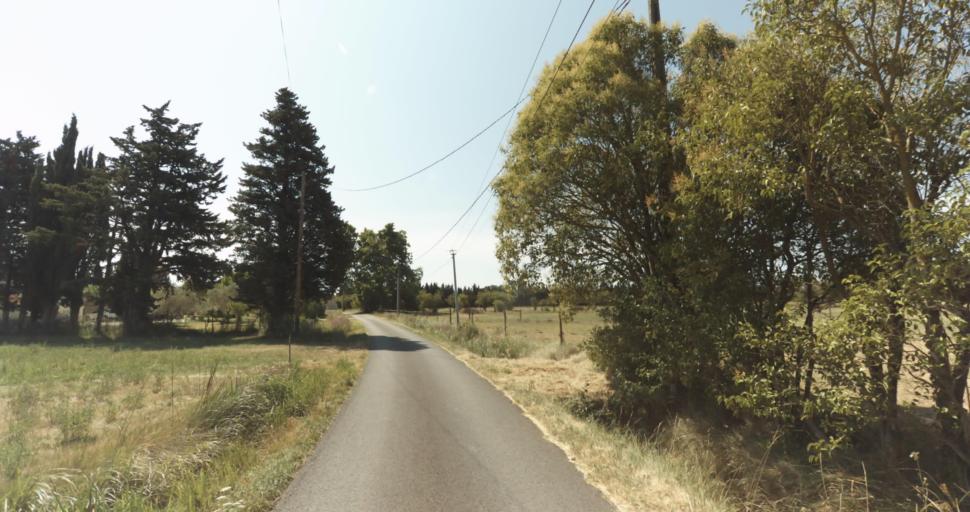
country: FR
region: Provence-Alpes-Cote d'Azur
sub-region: Departement du Vaucluse
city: Monteux
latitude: 44.0192
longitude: 4.9978
